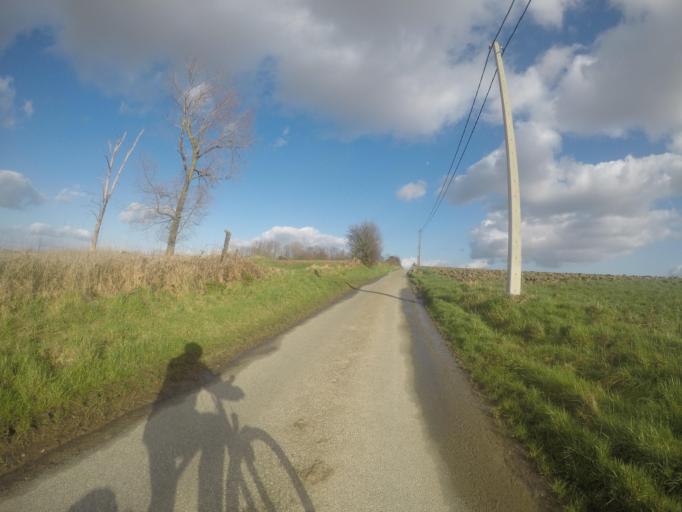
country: BE
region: Wallonia
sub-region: Province du Brabant Wallon
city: Rebecq-Rognon
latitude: 50.6464
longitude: 4.1008
